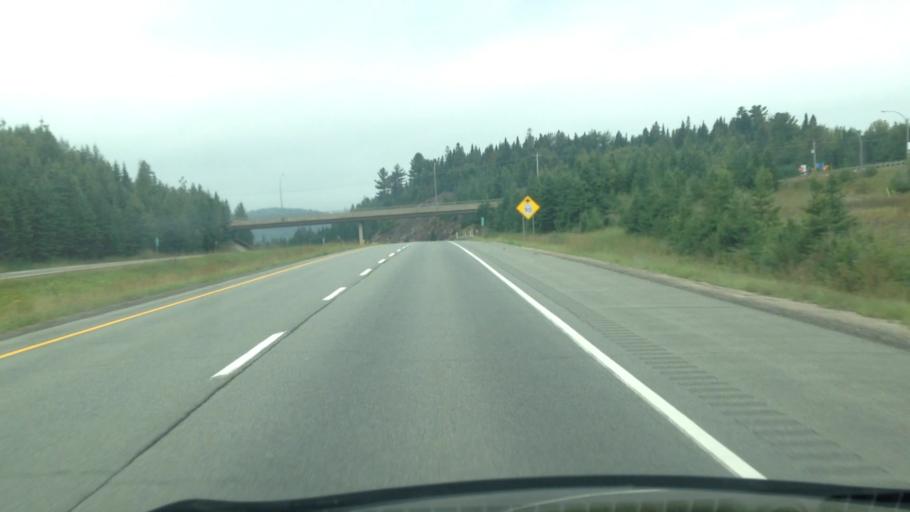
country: CA
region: Quebec
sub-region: Laurentides
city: Sainte-Agathe-des-Monts
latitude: 46.0628
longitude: -74.2860
